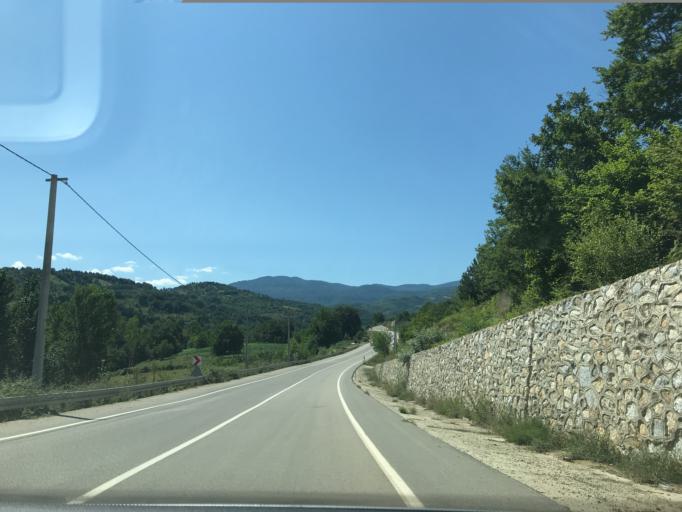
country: TR
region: Bursa
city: Tahtakopru
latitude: 39.9792
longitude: 29.6044
